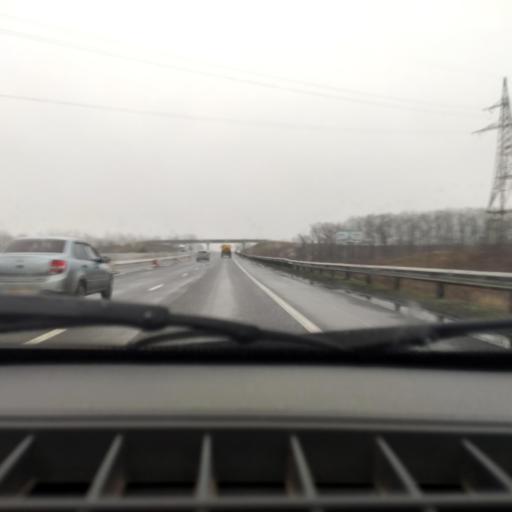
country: RU
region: Bashkortostan
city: Avdon
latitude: 54.6663
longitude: 55.7496
